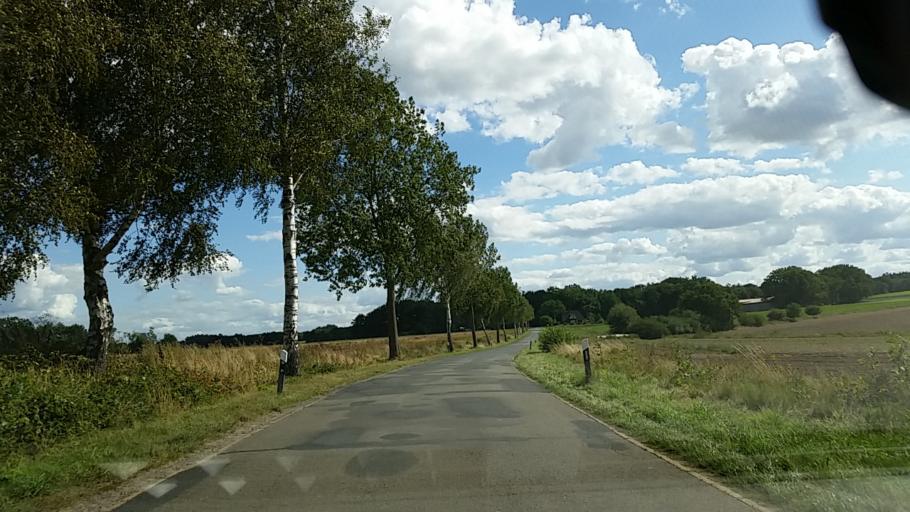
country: DE
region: Lower Saxony
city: Natendorf
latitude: 53.1230
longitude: 10.4307
